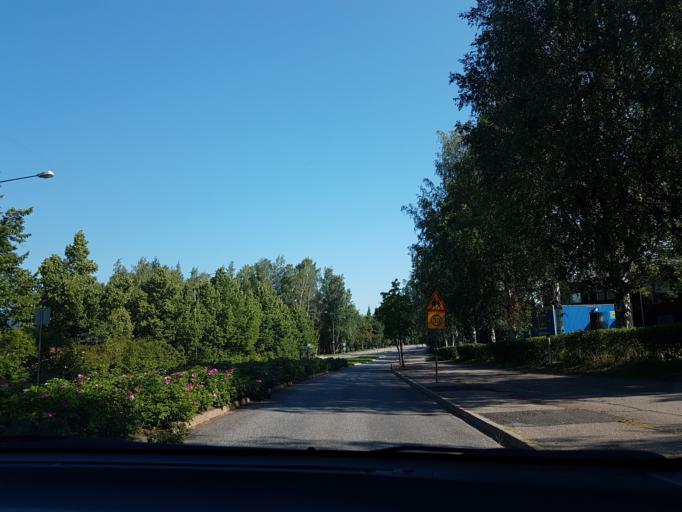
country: FI
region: Uusimaa
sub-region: Helsinki
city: Vantaa
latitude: 60.2659
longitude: 25.0580
